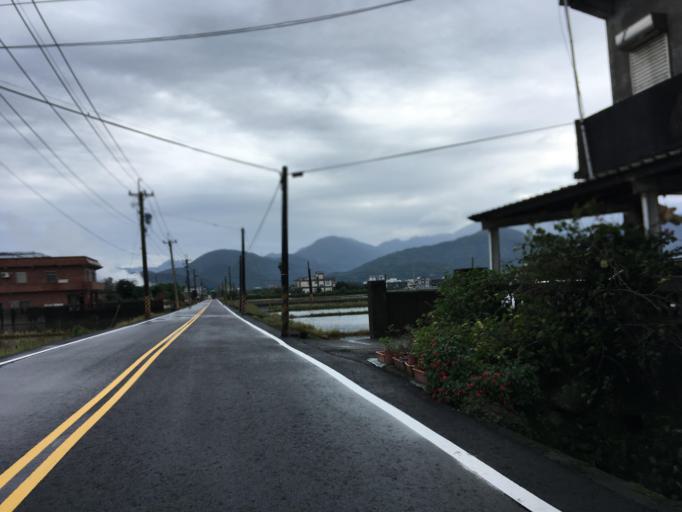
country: TW
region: Taiwan
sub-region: Yilan
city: Yilan
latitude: 24.6414
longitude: 121.8077
